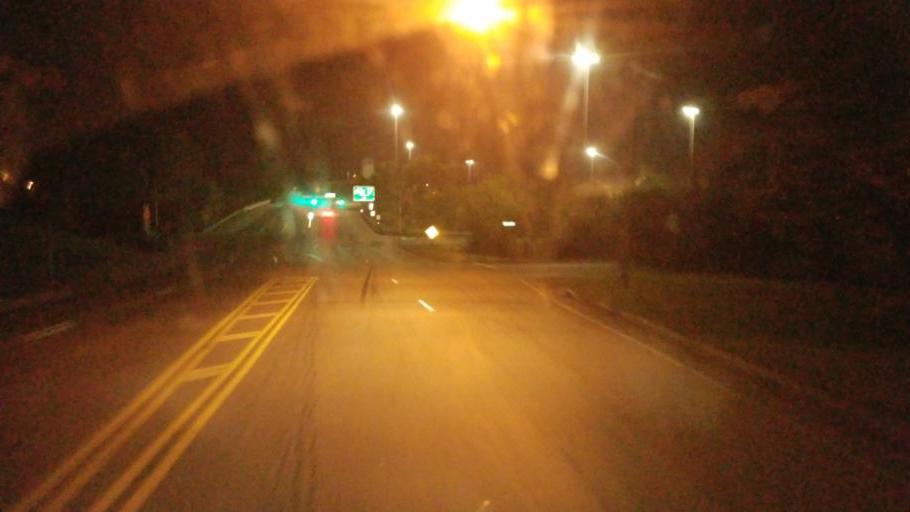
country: US
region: Ohio
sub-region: Wayne County
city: Wooster
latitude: 40.7878
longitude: -81.9342
